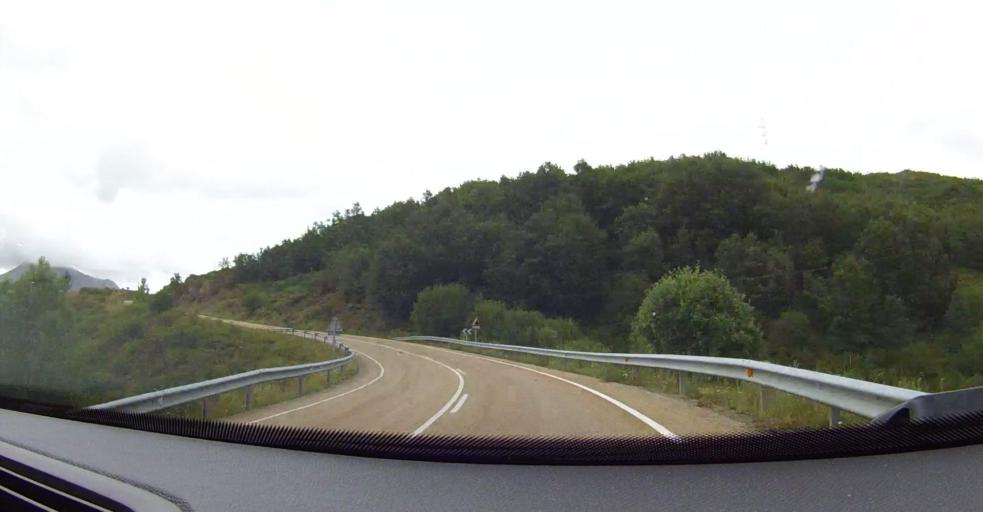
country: ES
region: Castille and Leon
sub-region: Provincia de Leon
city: Puebla de Lillo
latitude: 42.9336
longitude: -5.2725
